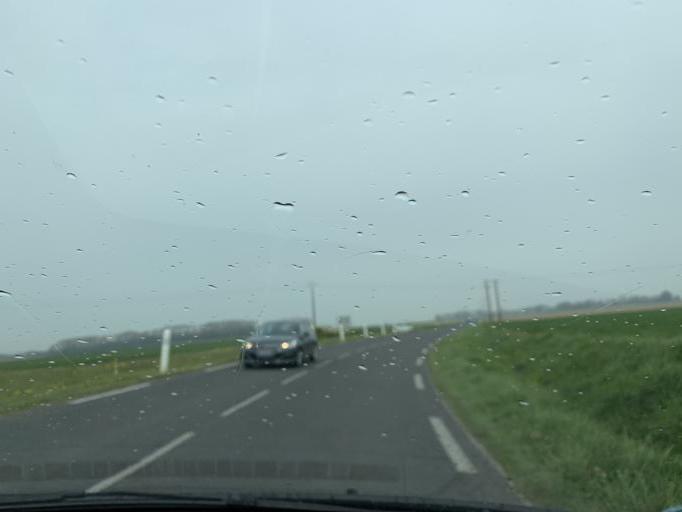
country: FR
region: Haute-Normandie
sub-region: Departement de la Seine-Maritime
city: Cany-Barville
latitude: 49.7897
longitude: 0.6563
